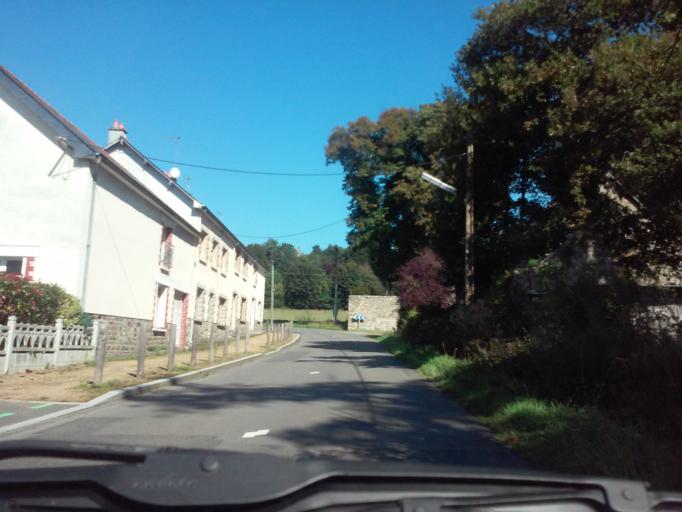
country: FR
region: Brittany
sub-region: Departement d'Ille-et-Vilaine
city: Saint-Medard-sur-Ille
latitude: 48.2458
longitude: -1.6549
